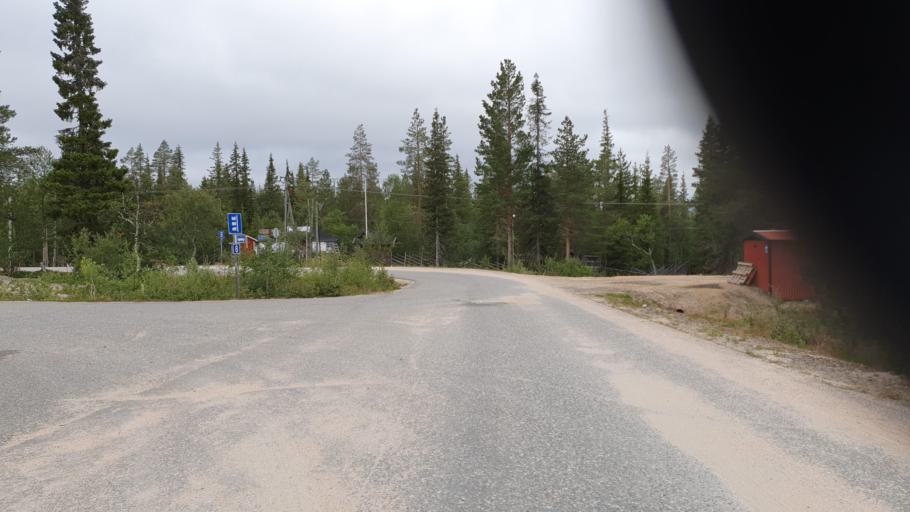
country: FI
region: Lapland
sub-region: Tunturi-Lappi
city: Kolari
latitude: 67.5828
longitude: 24.2059
